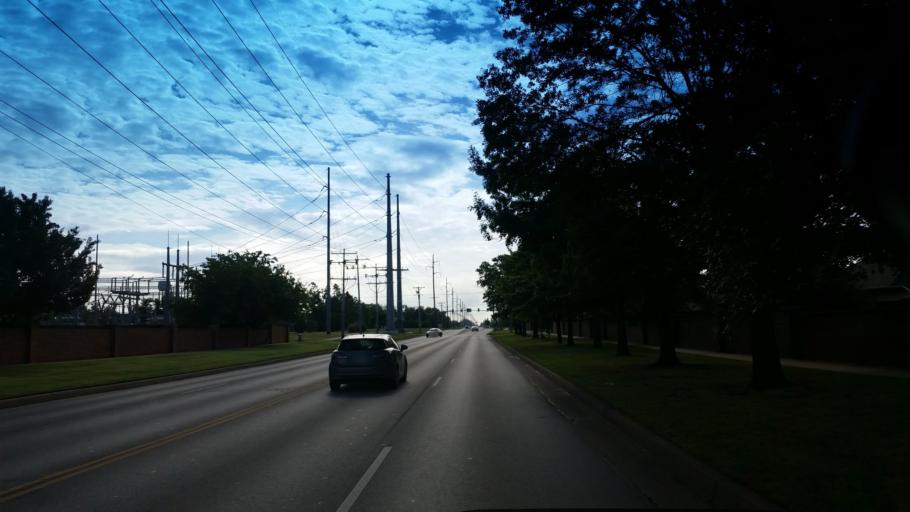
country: US
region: Oklahoma
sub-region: Oklahoma County
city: Edmond
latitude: 35.6675
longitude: -97.5072
